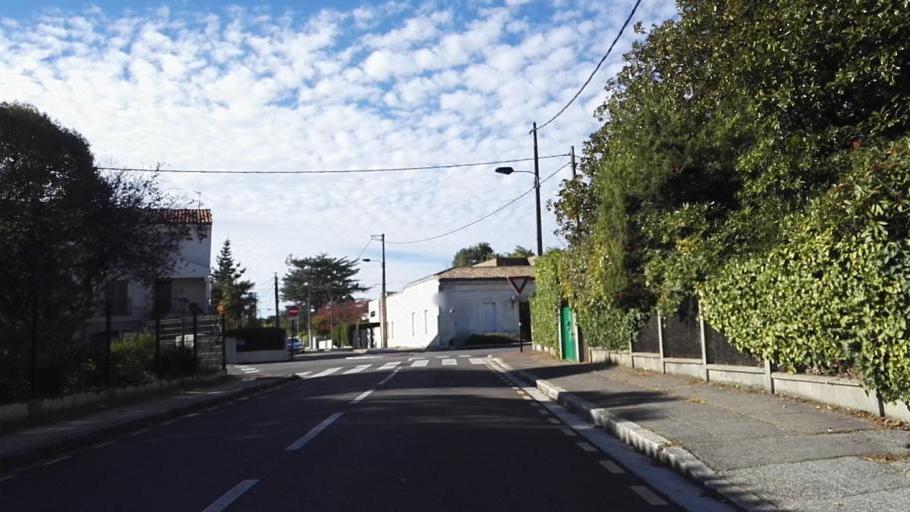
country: FR
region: Aquitaine
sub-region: Departement de la Gironde
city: Bruges
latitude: 44.8617
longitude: -0.6230
